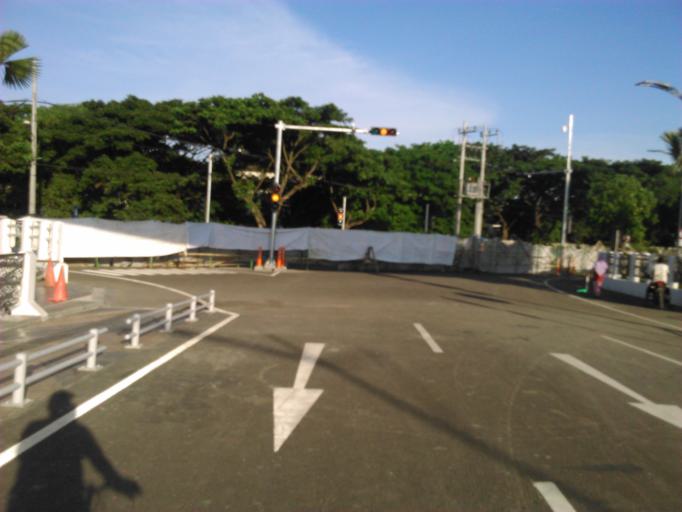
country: ID
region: East Java
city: Labansari
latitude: -7.2354
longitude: 112.7954
